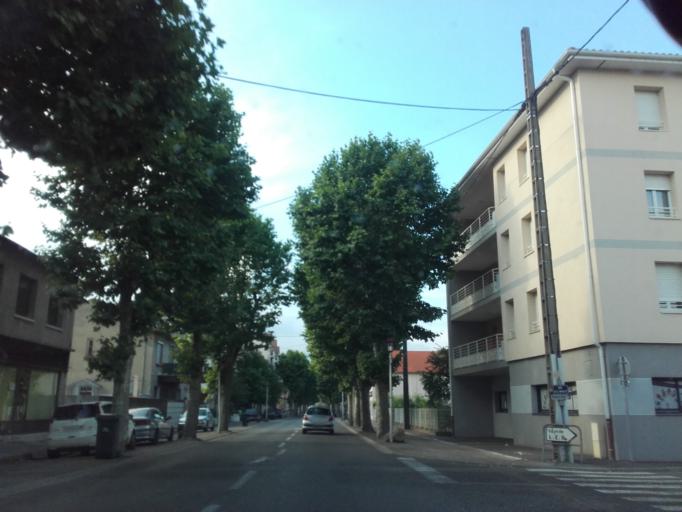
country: FR
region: Rhone-Alpes
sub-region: Departement de l'Isere
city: Le Peage-de-Roussillon
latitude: 45.3650
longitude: 4.8003
